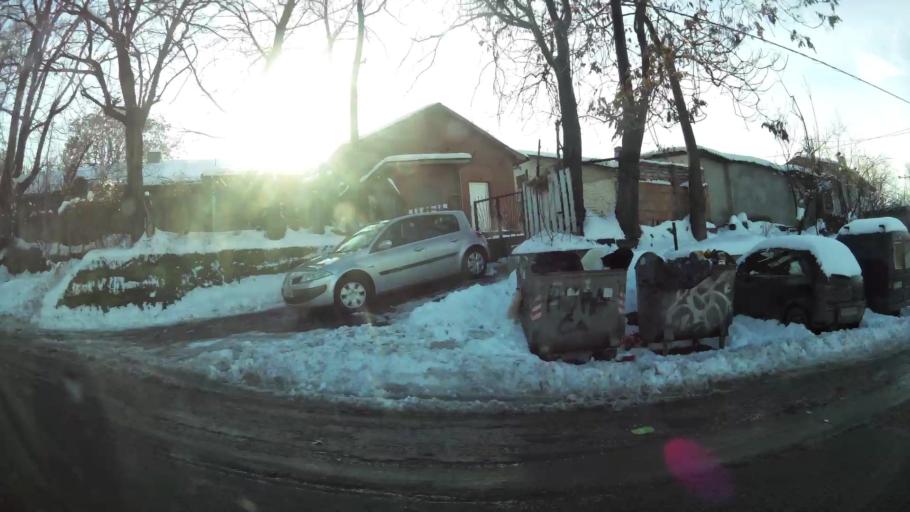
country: RS
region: Central Serbia
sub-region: Belgrade
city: Palilula
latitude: 44.8189
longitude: 20.4950
